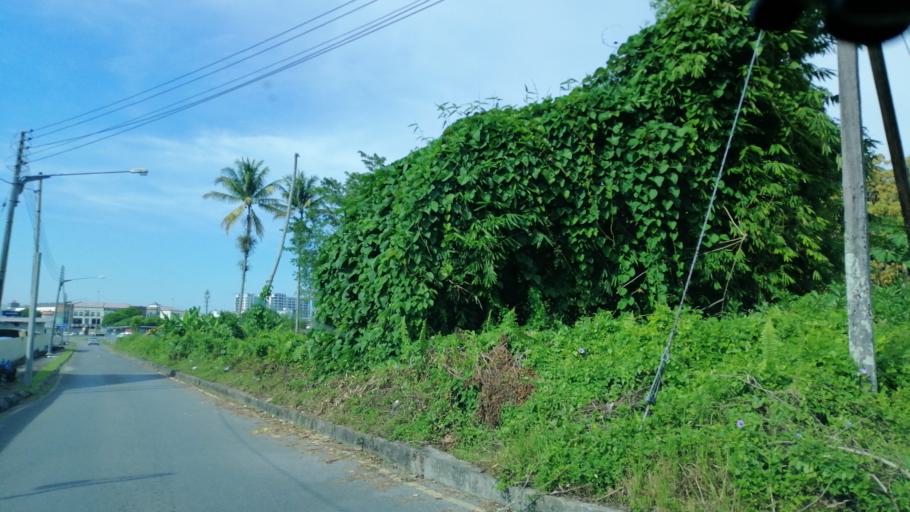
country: MY
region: Sarawak
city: Kuching
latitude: 1.5194
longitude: 110.3526
